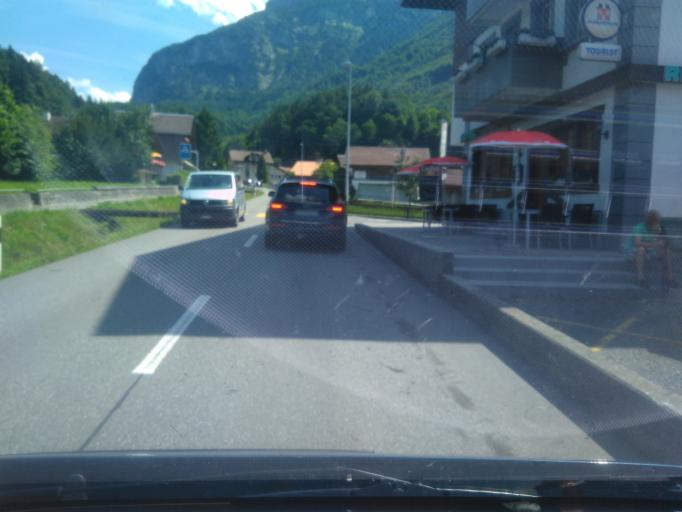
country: CH
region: Bern
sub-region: Interlaken-Oberhasli District
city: Meiringen
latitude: 46.7193
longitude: 8.1905
